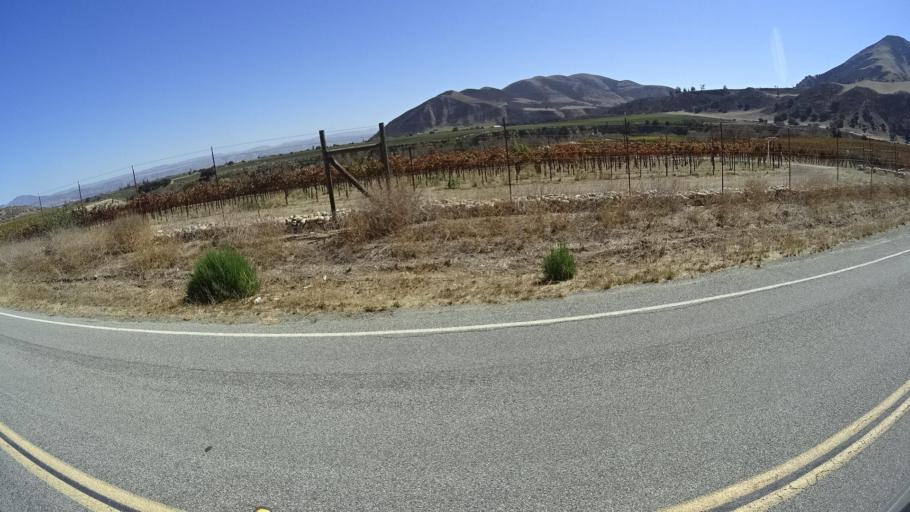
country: US
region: California
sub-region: Monterey County
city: Greenfield
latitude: 36.2851
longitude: -121.3210
